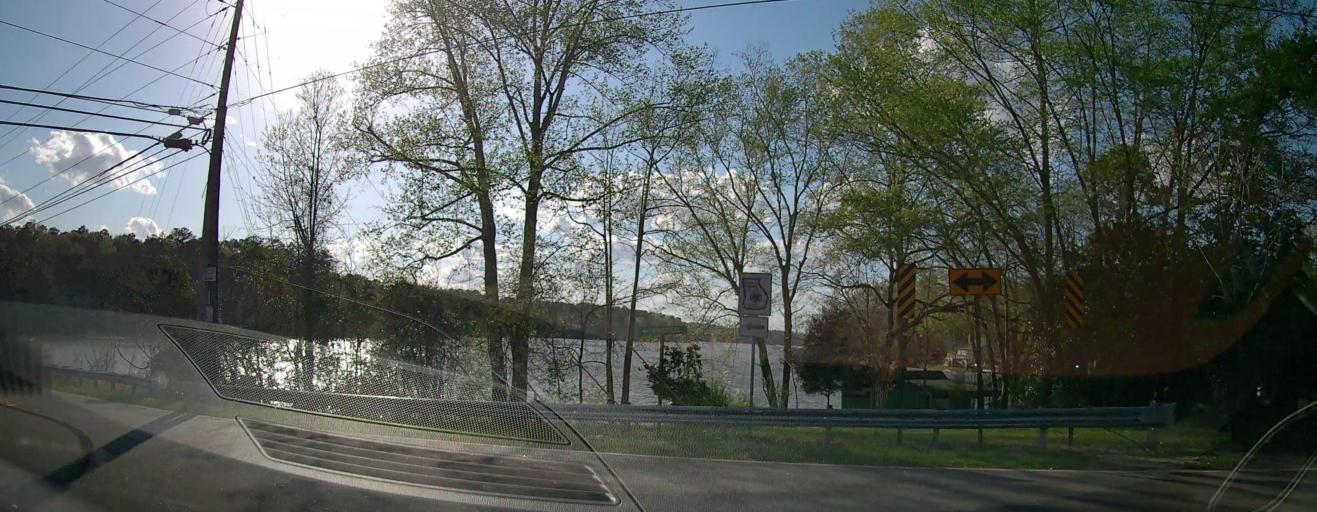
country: US
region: Georgia
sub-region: Putnam County
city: Eatonton
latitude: 33.2037
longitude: -83.3794
